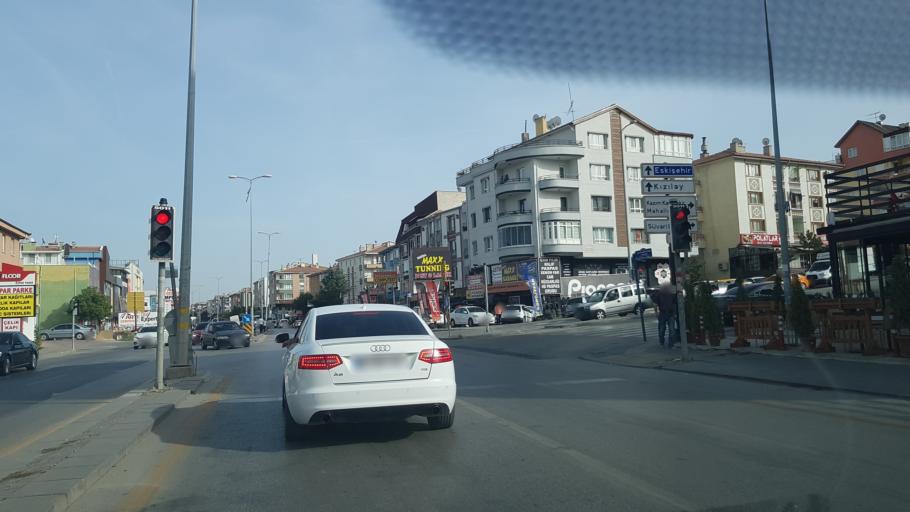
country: TR
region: Ankara
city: Etimesgut
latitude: 39.9513
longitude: 32.6487
